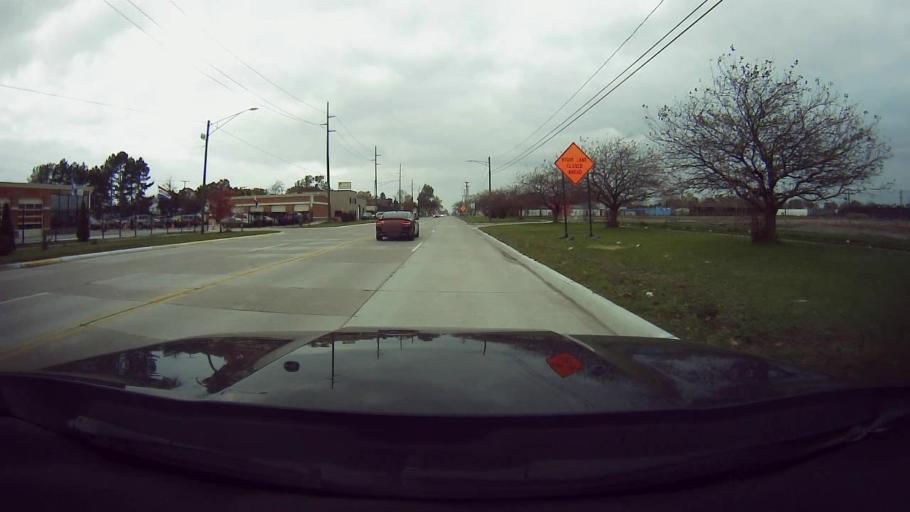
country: US
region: Michigan
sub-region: Macomb County
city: Eastpointe
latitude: 42.4504
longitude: -82.9856
